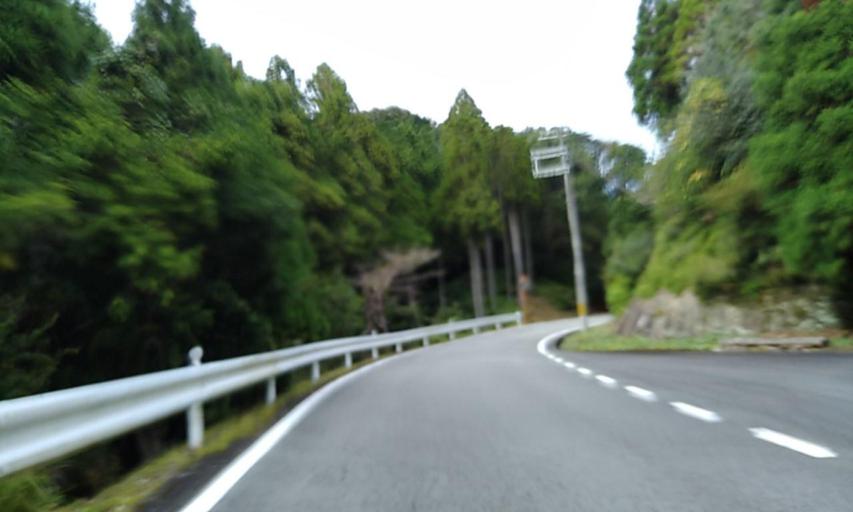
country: JP
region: Wakayama
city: Shingu
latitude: 33.5438
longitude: 135.8454
